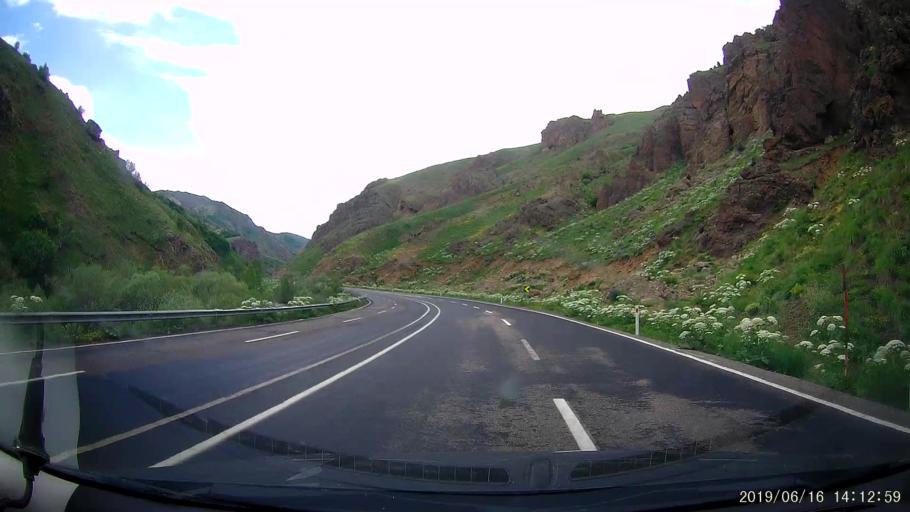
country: TR
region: Agri
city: Tahir
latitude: 39.7996
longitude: 42.5260
